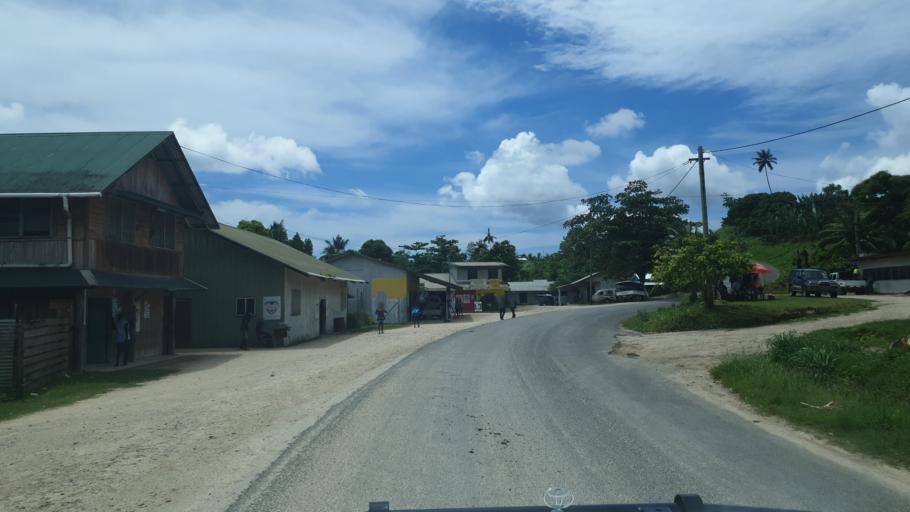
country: PG
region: Bougainville
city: Buka
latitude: -5.4342
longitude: 154.6752
